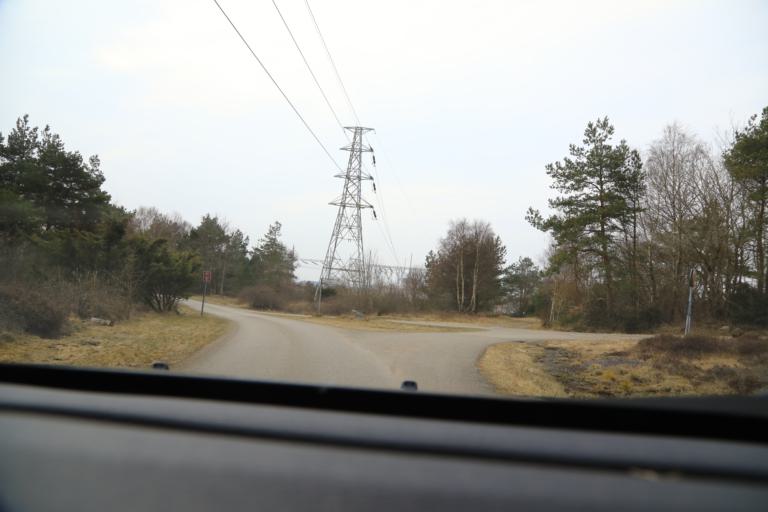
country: SE
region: Halland
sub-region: Kungsbacka Kommun
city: Frillesas
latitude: 57.2636
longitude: 12.1216
